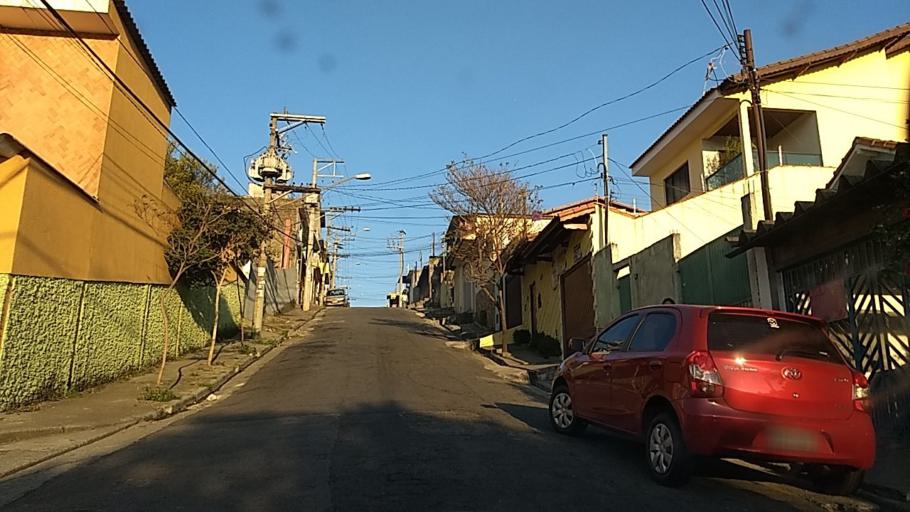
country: BR
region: Sao Paulo
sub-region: Sao Paulo
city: Sao Paulo
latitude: -23.4946
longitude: -46.5946
